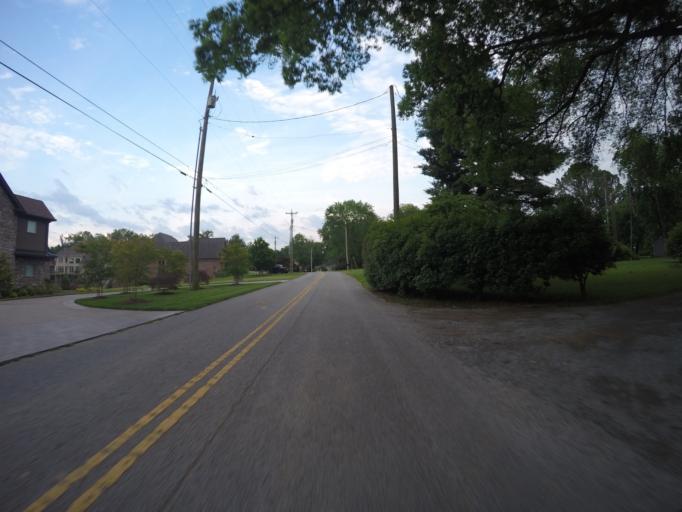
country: US
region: Tennessee
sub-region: Davidson County
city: Lakewood
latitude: 36.2444
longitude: -86.6317
